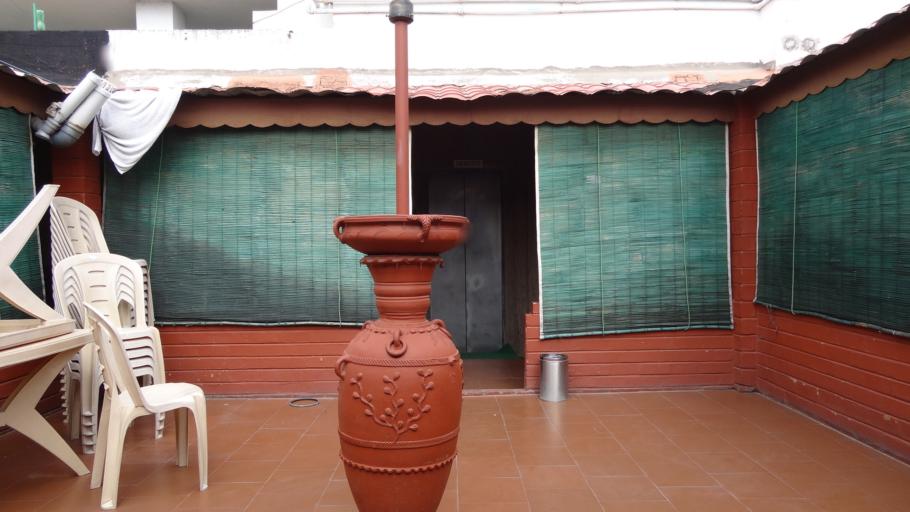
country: IN
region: Karnataka
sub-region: Mysore
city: Mysore
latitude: 12.3209
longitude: 76.6475
